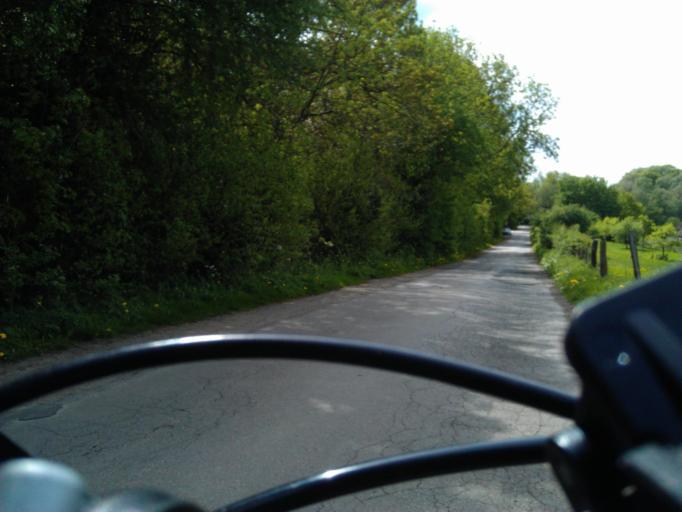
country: NL
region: Limburg
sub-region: Gemeente Vaals
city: Vaals
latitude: 50.7629
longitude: 6.0342
